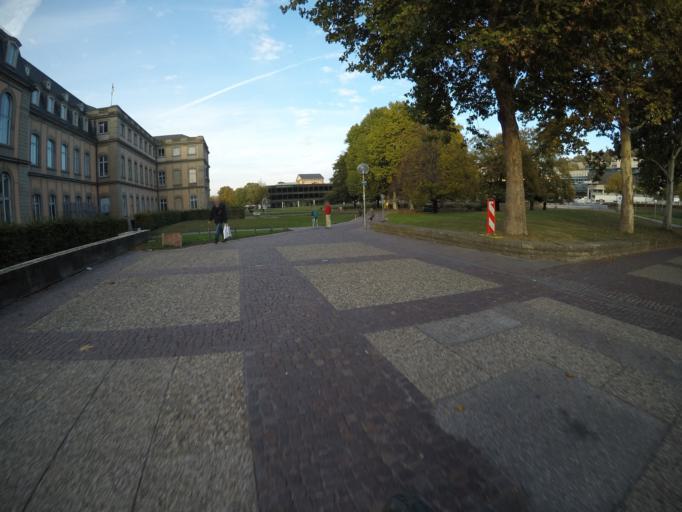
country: DE
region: Baden-Wuerttemberg
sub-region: Regierungsbezirk Stuttgart
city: Stuttgart
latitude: 48.7772
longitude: 9.1818
